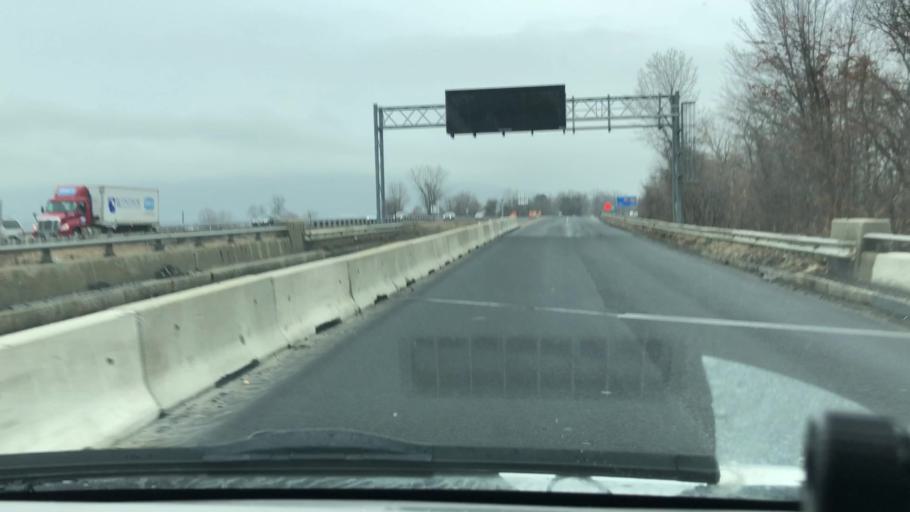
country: US
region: Massachusetts
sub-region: Hampshire County
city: Northampton
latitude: 42.3277
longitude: -72.6170
